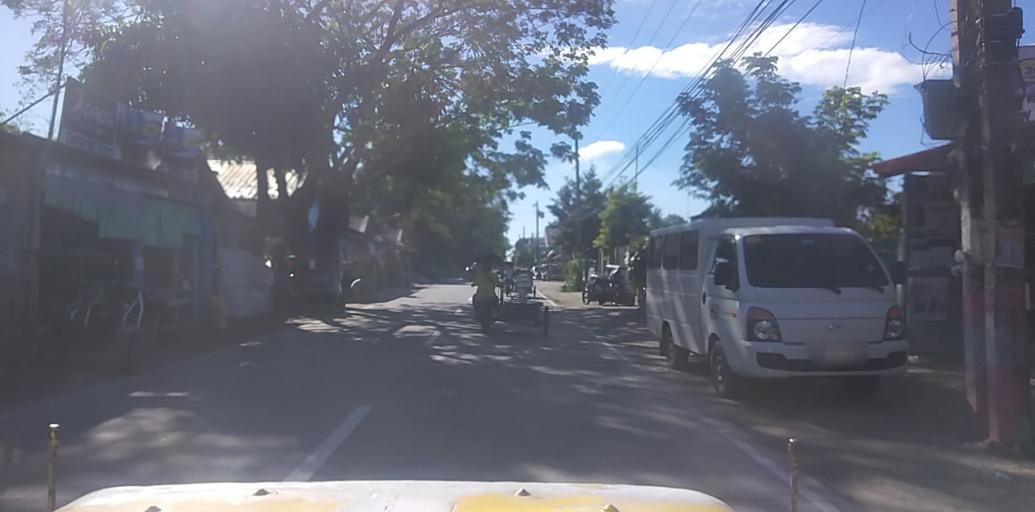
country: PH
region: Central Luzon
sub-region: Province of Pampanga
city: San Patricio
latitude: 15.0895
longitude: 120.7135
